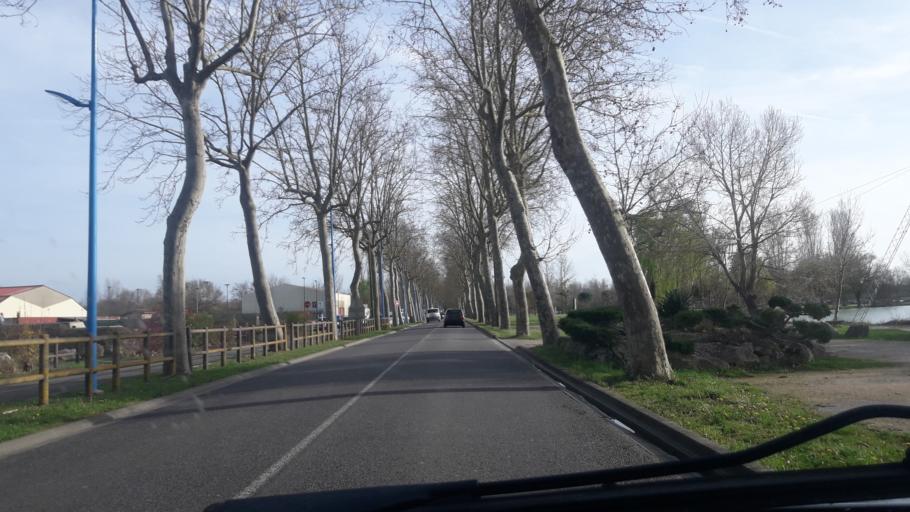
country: FR
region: Midi-Pyrenees
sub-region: Departement du Gers
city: Pujaudran
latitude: 43.6189
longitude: 1.0727
